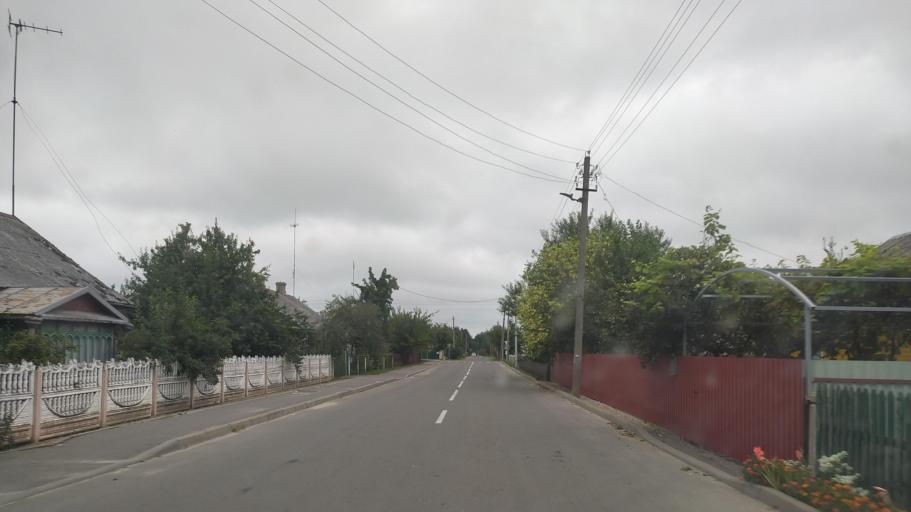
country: BY
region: Brest
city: Byaroza
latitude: 52.5317
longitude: 24.9686
